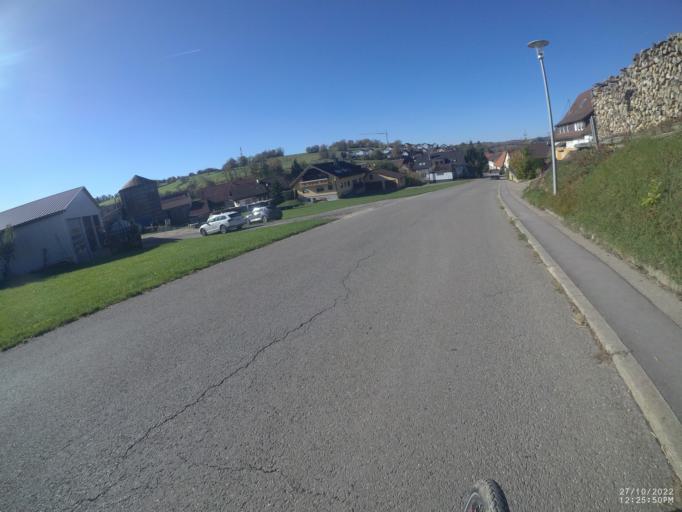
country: DE
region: Baden-Wuerttemberg
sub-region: Regierungsbezirk Stuttgart
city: Hohenstadt
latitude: 48.5569
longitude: 9.6831
